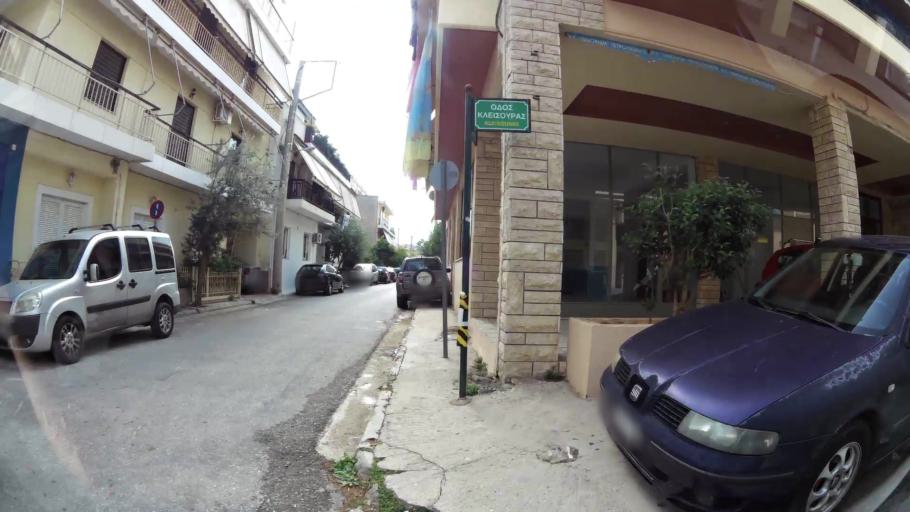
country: GR
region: Attica
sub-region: Nomarchia Athinas
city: Petroupolis
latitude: 38.0451
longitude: 23.6952
